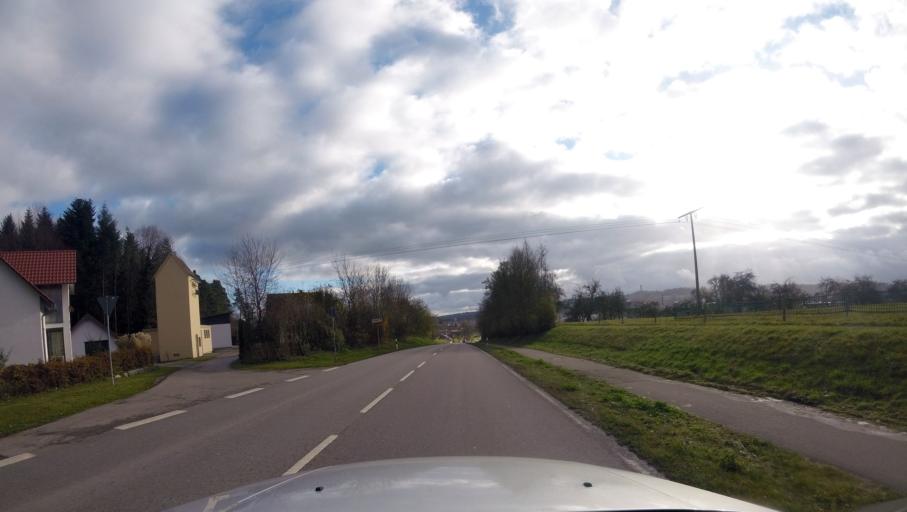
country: DE
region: Baden-Wuerttemberg
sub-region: Regierungsbezirk Stuttgart
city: Gschwend
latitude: 48.9435
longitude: 9.7409
